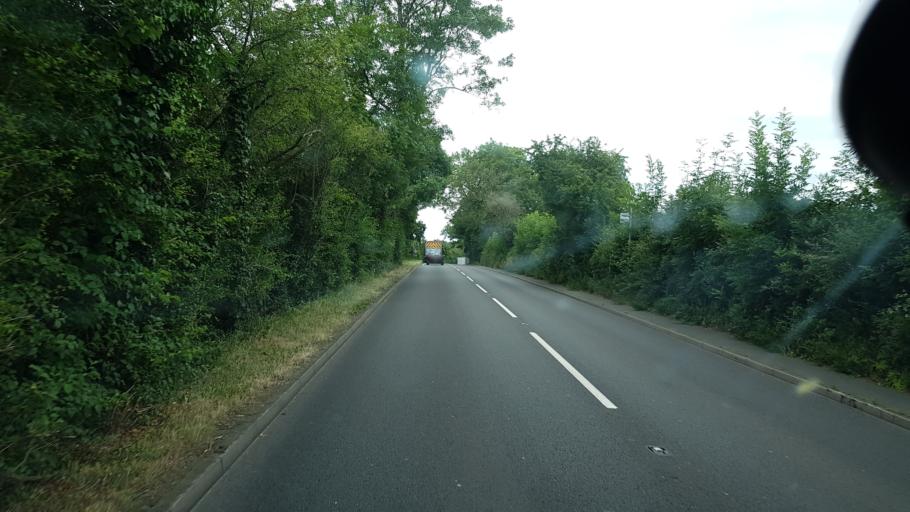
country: GB
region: England
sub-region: Surrey
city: Godstone
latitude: 51.2095
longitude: -0.0545
